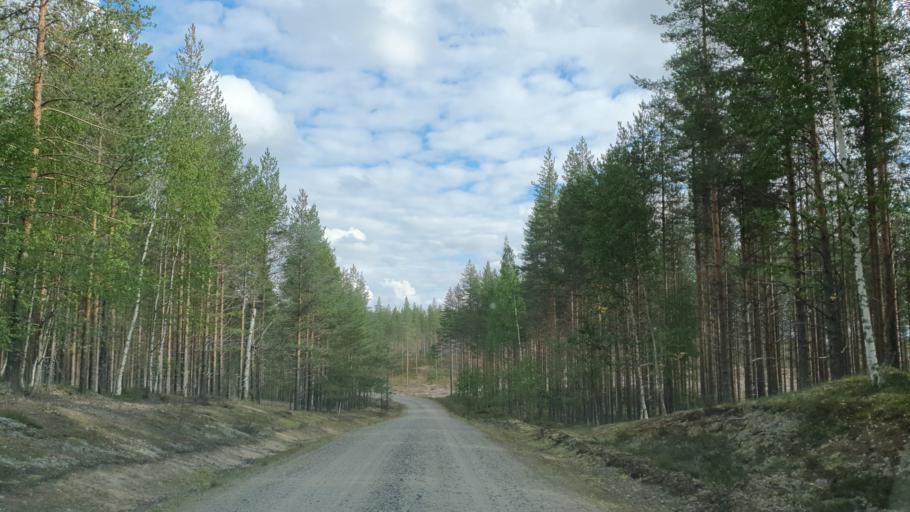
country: FI
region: Kainuu
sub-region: Kehys-Kainuu
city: Kuhmo
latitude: 64.2092
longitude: 29.1700
